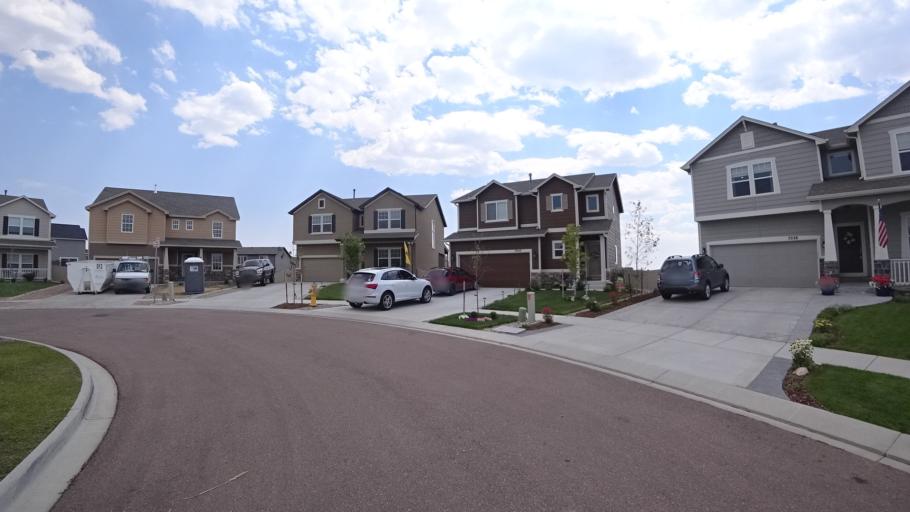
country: US
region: Colorado
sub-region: El Paso County
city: Black Forest
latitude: 38.9538
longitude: -104.6956
